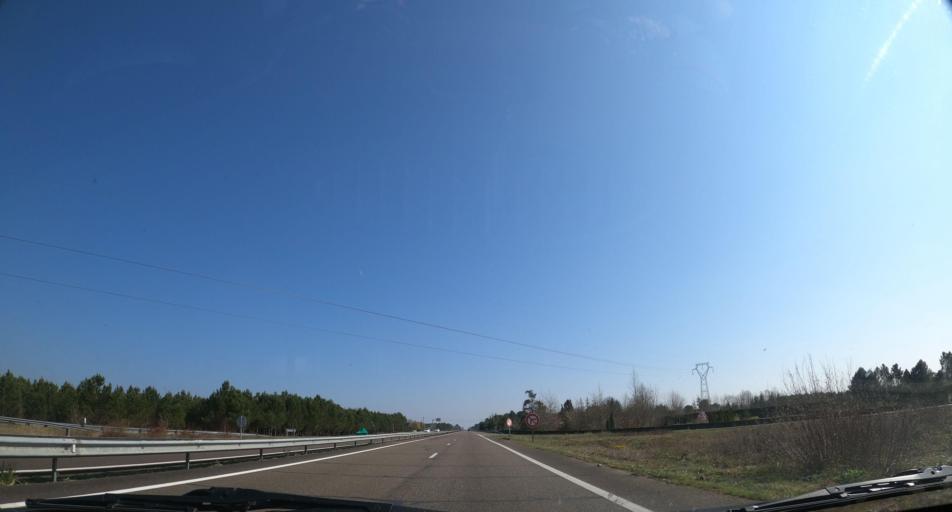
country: FR
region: Aquitaine
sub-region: Departement des Landes
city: Saint-Perdon
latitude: 43.8734
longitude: -0.5819
